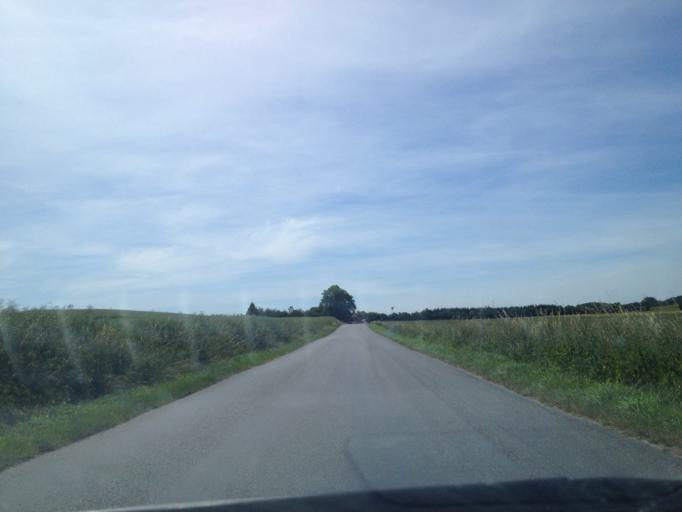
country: DK
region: Central Jutland
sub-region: Samso Kommune
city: Tranebjerg
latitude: 55.8436
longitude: 10.6200
